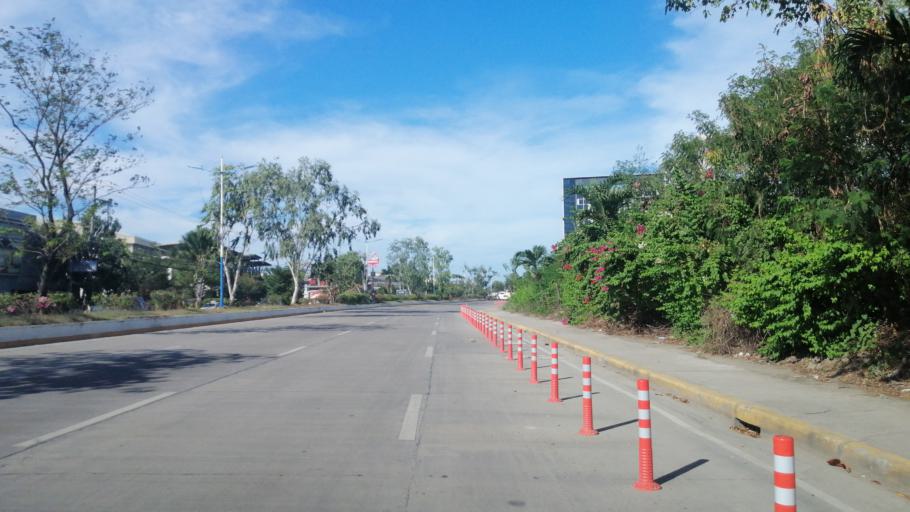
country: PH
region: Central Visayas
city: Mandaue City
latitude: 10.3230
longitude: 123.9340
